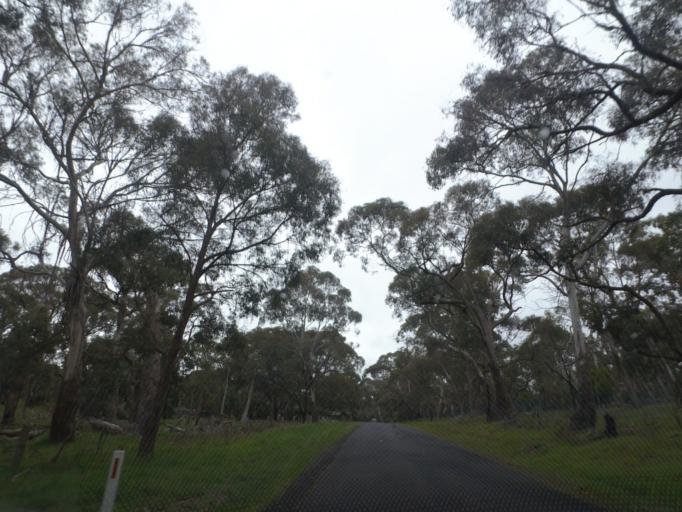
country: AU
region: Victoria
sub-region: Hume
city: Sunbury
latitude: -37.3276
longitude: 144.5942
